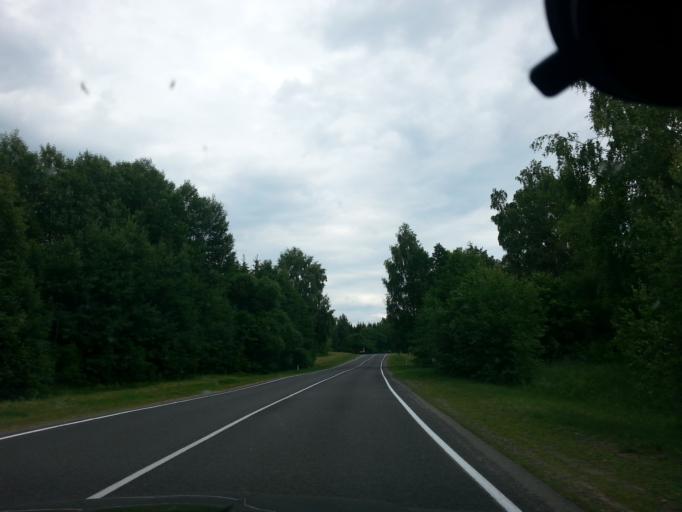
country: BY
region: Minsk
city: Narach
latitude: 54.9053
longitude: 26.7447
